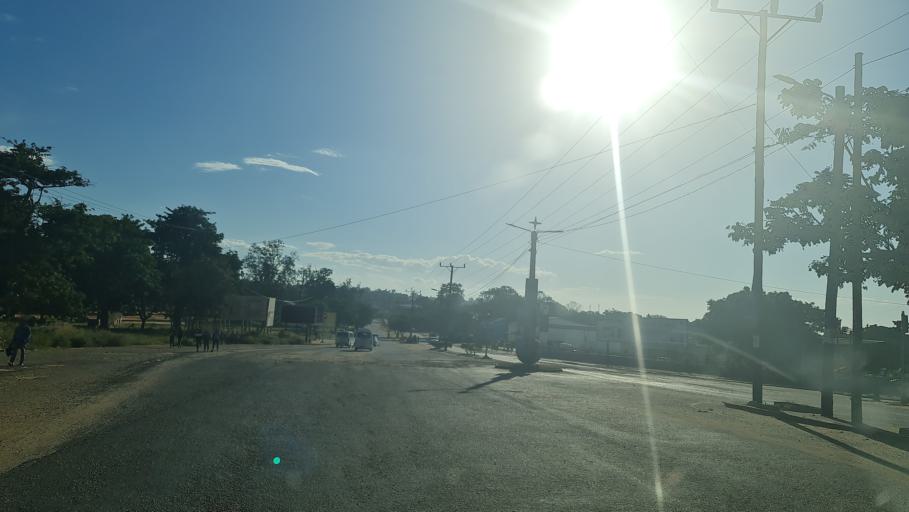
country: MZ
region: Cabo Delgado
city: Pemba
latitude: -12.9679
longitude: 40.5125
